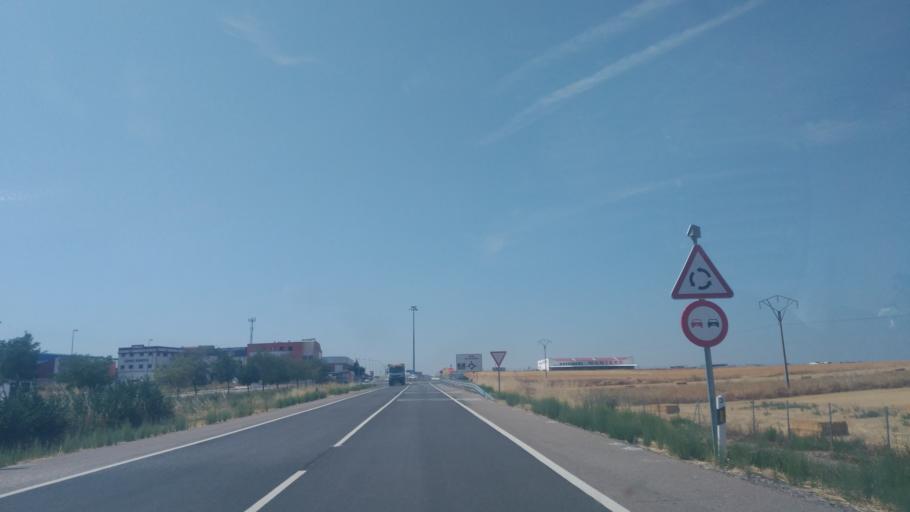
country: ES
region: Castille and Leon
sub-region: Provincia de Salamanca
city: Castellanos de Moriscos
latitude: 41.0113
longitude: -5.6089
